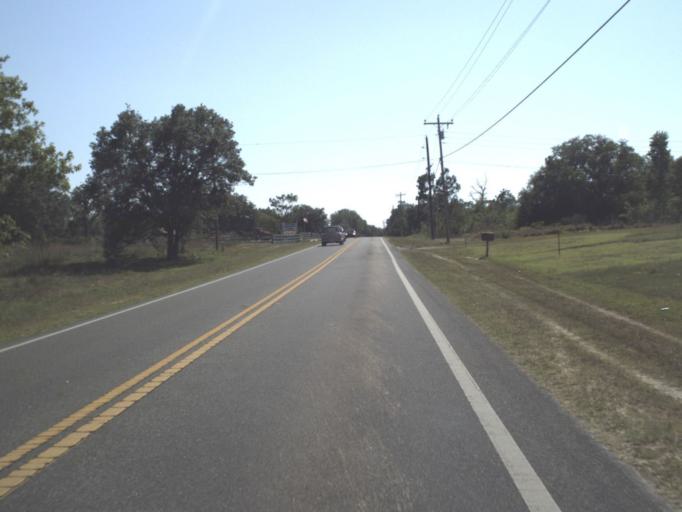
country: US
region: Florida
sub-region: Marion County
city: Dunnellon
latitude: 29.1339
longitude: -82.3995
